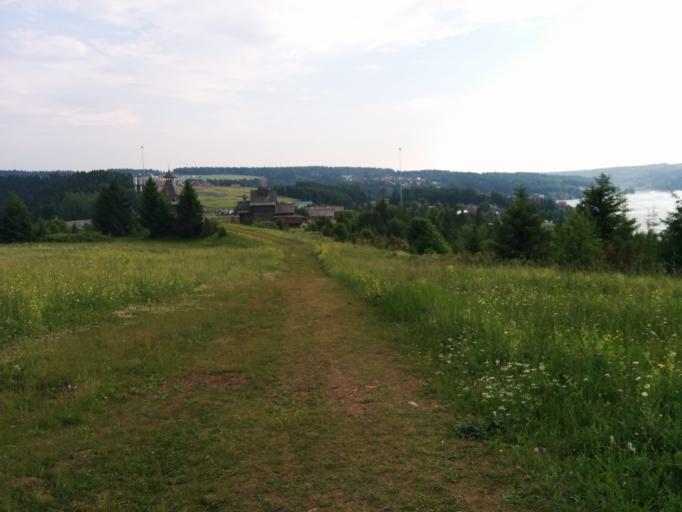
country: RU
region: Perm
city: Polazna
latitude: 58.2624
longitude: 56.2606
